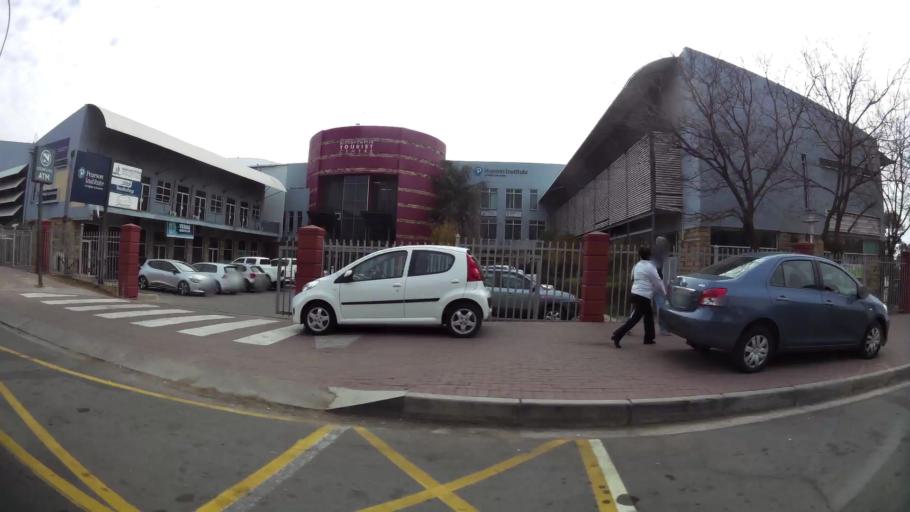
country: ZA
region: Orange Free State
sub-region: Mangaung Metropolitan Municipality
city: Bloemfontein
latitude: -29.1200
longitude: 26.2071
